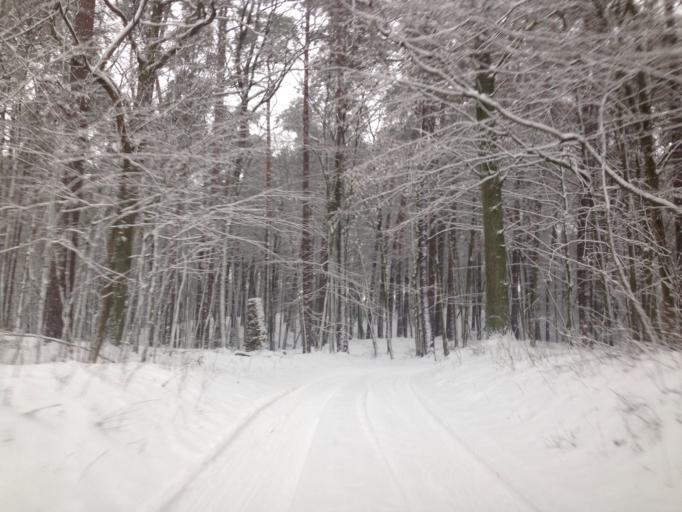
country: PL
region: Kujawsko-Pomorskie
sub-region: Powiat brodnicki
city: Gorzno
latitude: 53.1880
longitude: 19.6620
